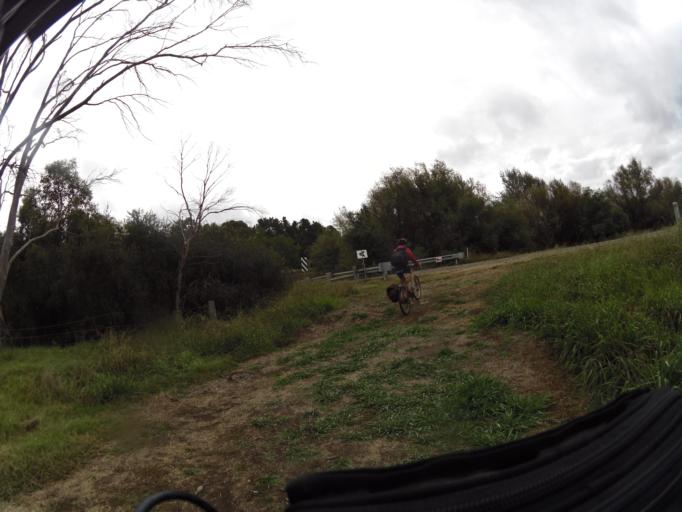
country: AU
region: New South Wales
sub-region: Albury Municipality
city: East Albury
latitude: -36.1941
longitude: 147.3108
